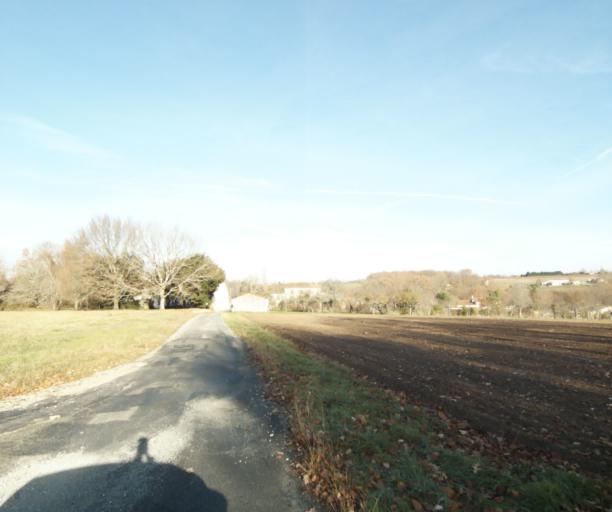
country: FR
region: Poitou-Charentes
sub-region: Departement de la Charente-Maritime
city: Burie
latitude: 45.7561
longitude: -0.4840
